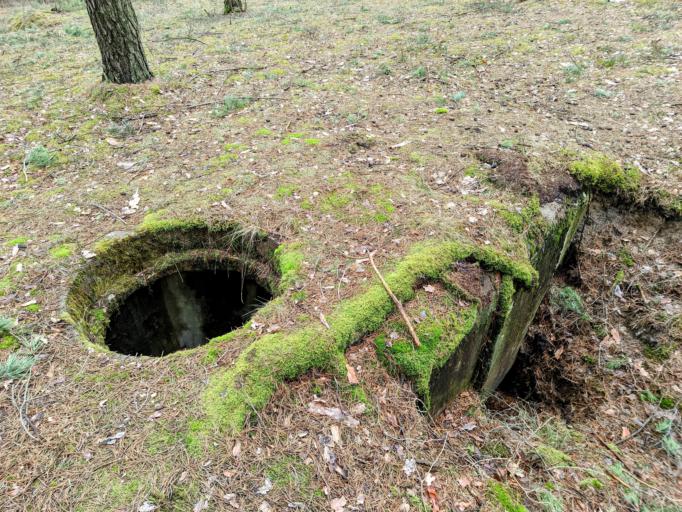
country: PL
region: Lubusz
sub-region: Powiat swiebodzinski
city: Skape
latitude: 52.1692
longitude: 15.4265
